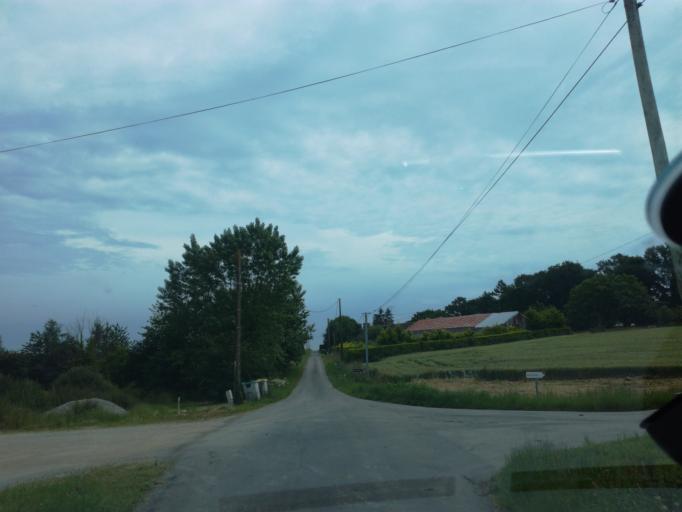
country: FR
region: Brittany
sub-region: Departement du Morbihan
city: Saint-Thuriau
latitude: 48.0165
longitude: -2.9158
